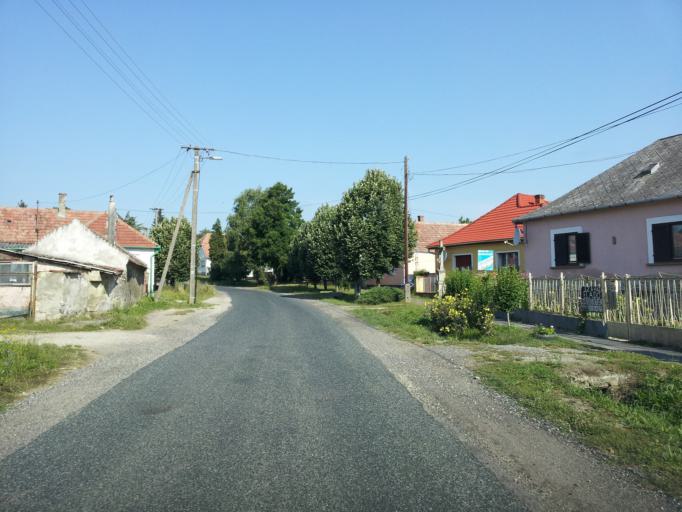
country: HU
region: Zala
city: Cserszegtomaj
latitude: 46.8829
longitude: 17.2308
